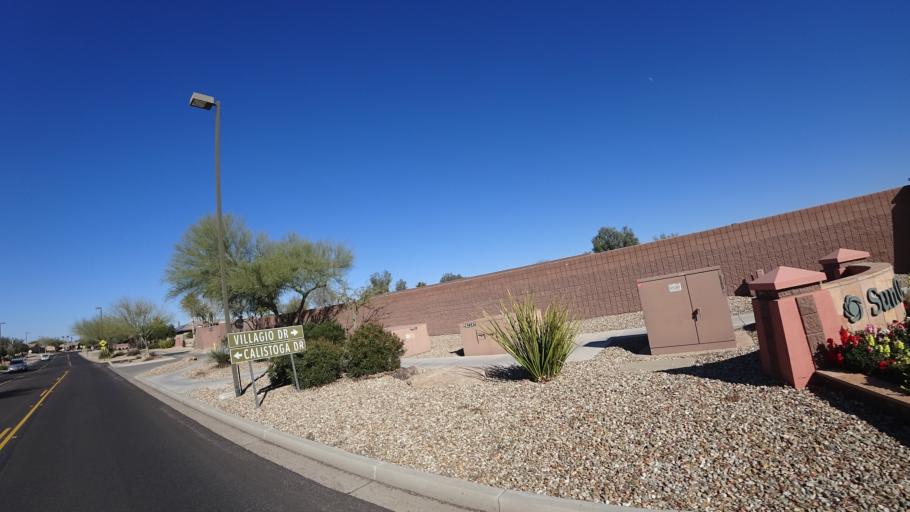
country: US
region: Arizona
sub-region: Maricopa County
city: Sun City West
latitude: 33.6534
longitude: -112.4268
